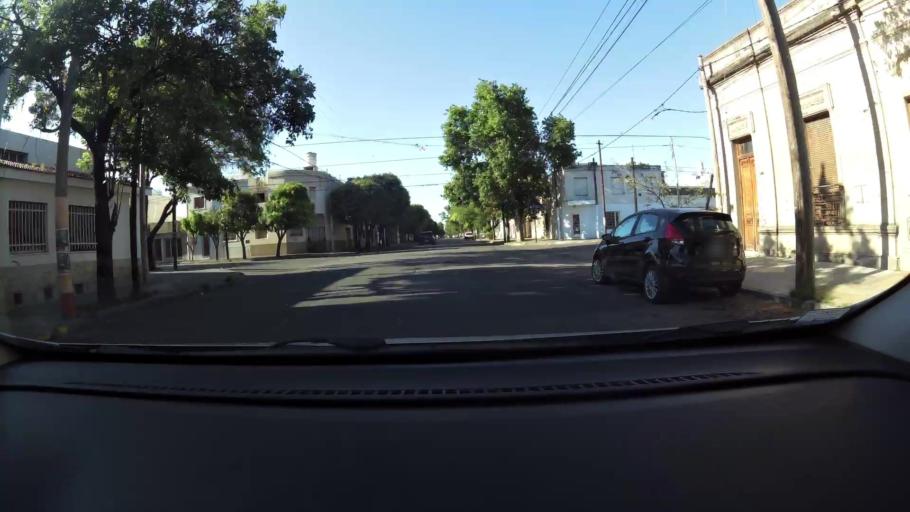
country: AR
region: Cordoba
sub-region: Departamento de Capital
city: Cordoba
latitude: -31.3890
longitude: -64.1824
